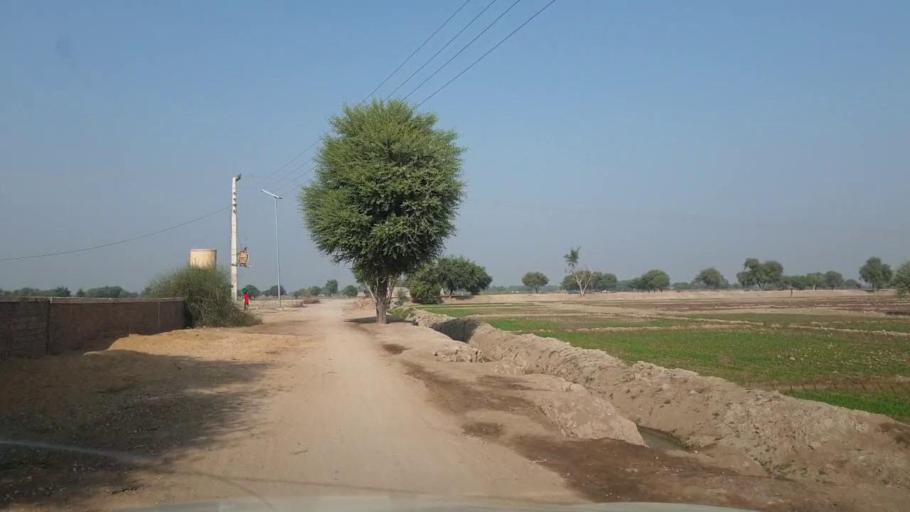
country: PK
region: Sindh
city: Bhan
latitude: 26.5084
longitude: 67.7942
